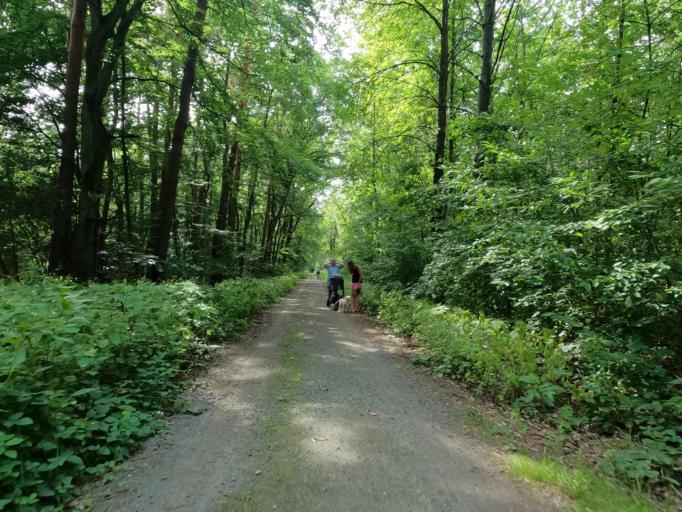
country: DE
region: Hesse
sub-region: Regierungsbezirk Darmstadt
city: Neu Isenburg
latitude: 50.0378
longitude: 8.6877
